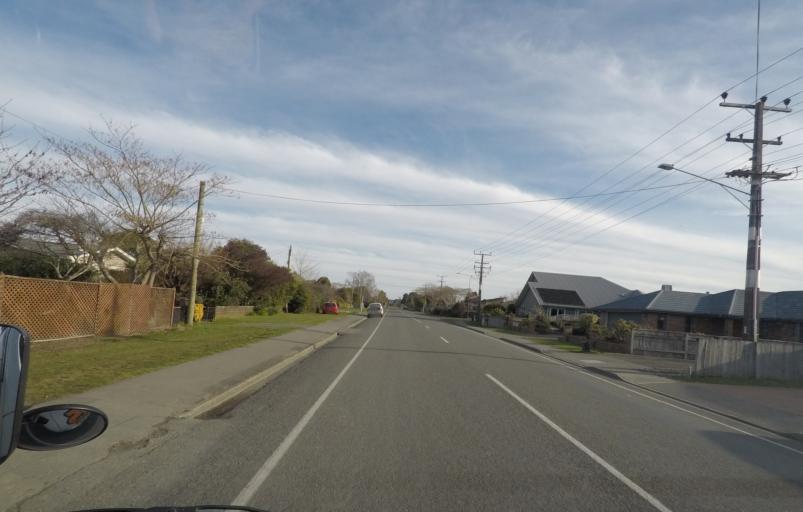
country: NZ
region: Tasman
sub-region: Tasman District
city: Brightwater
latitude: -41.3756
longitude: 173.1047
